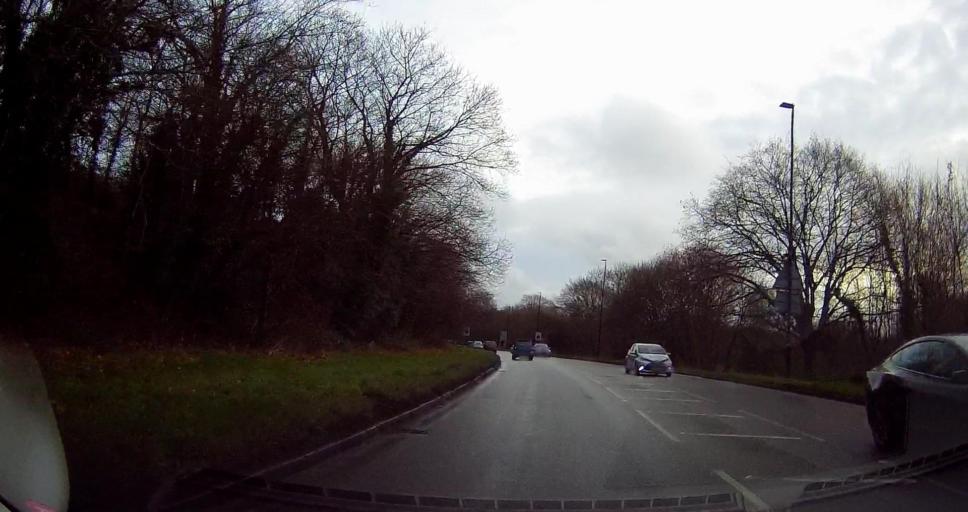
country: GB
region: England
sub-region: Greater London
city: Orpington
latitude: 51.3487
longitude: 0.0897
